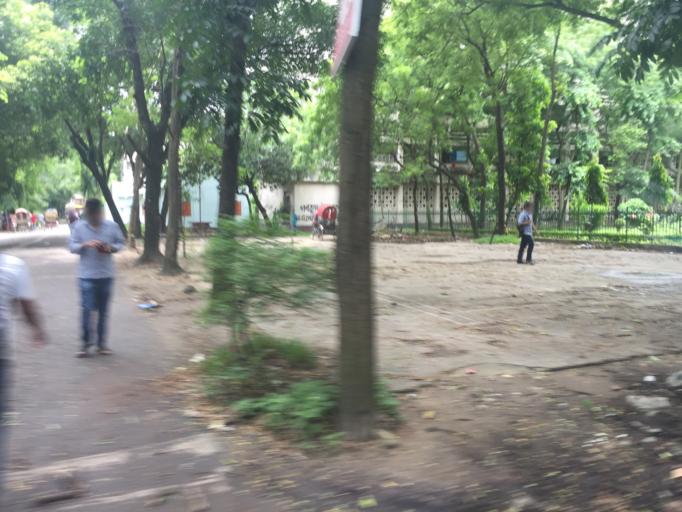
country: BD
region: Dhaka
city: Azimpur
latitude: 23.7357
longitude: 90.3915
